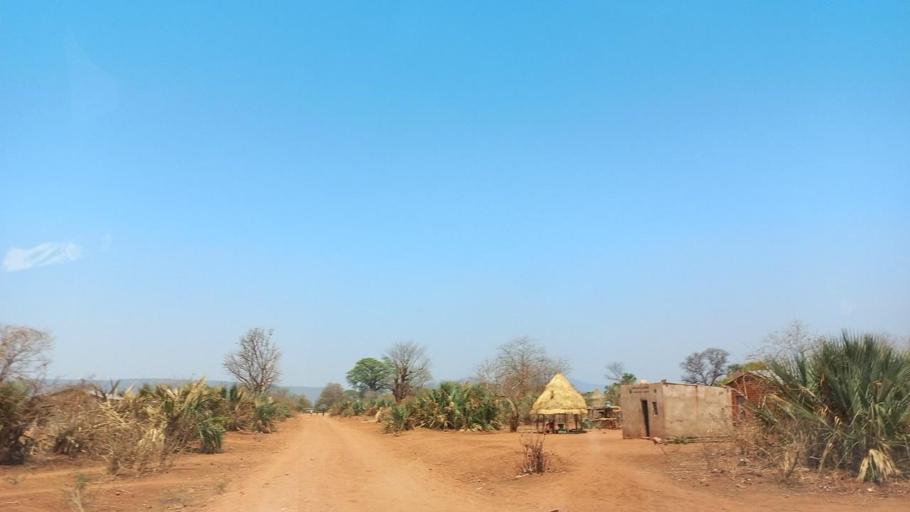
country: ZM
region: Lusaka
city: Luangwa
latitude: -15.1873
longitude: 30.2069
